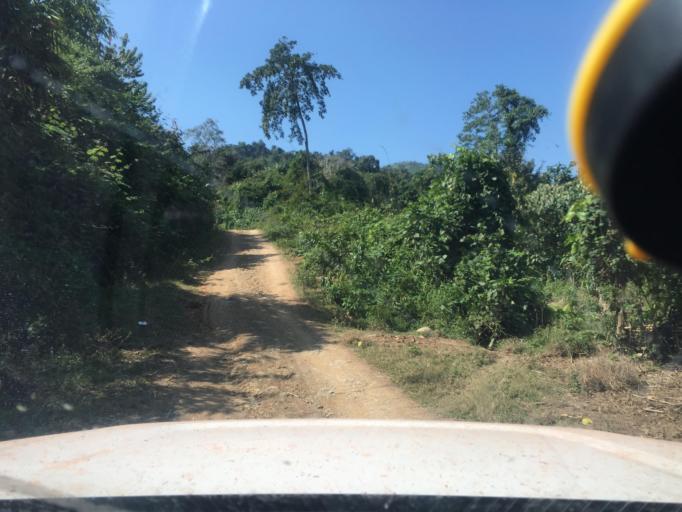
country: LA
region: Phongsali
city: Phongsali
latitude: 21.6588
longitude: 102.4196
